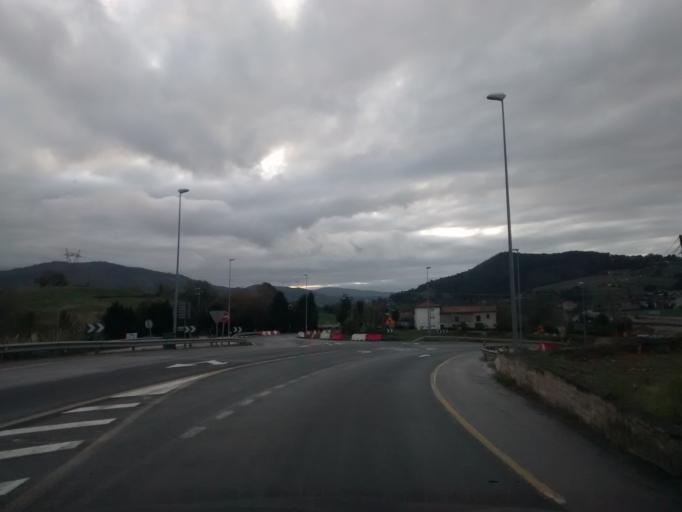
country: ES
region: Cantabria
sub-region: Provincia de Cantabria
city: Santa Maria de Cayon
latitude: 43.3317
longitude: -3.8402
